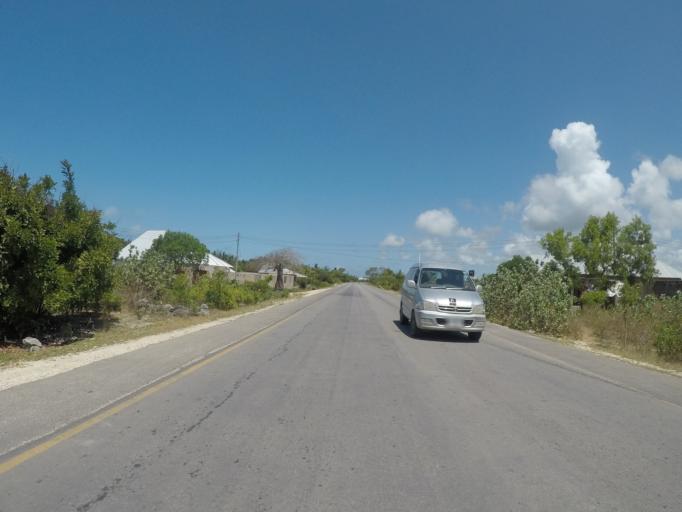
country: TZ
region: Zanzibar Central/South
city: Nganane
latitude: -6.3090
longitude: 39.5407
